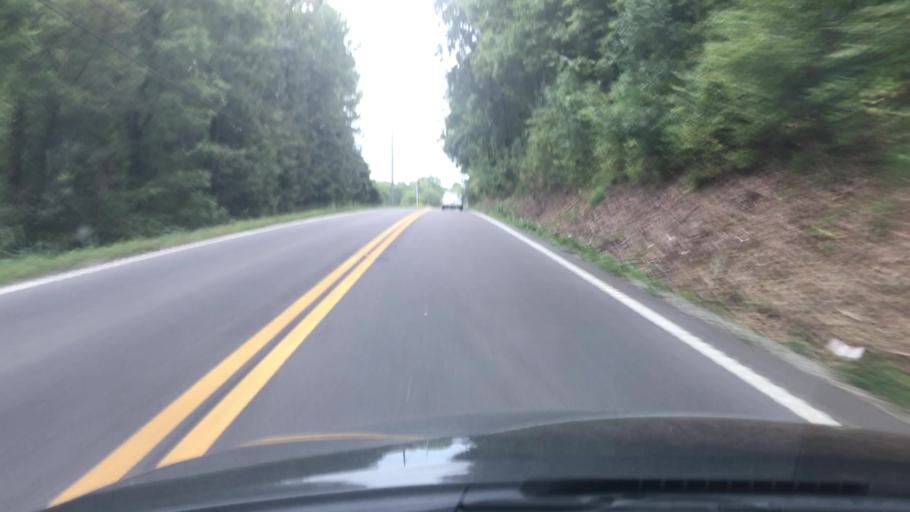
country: US
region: Tennessee
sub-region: Cheatham County
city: Ashland City
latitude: 36.2774
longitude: -87.0945
